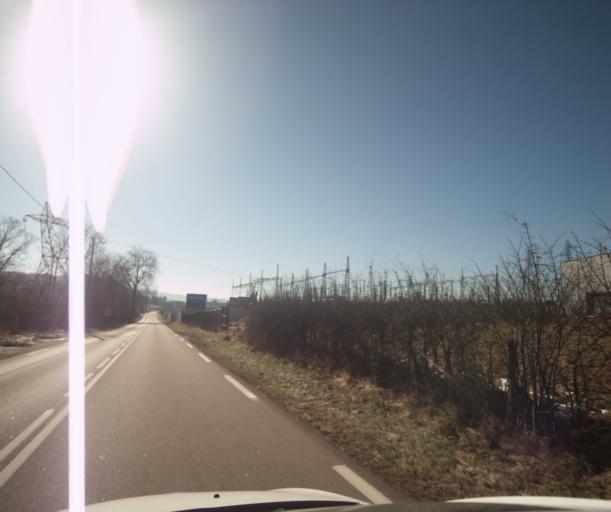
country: FR
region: Franche-Comte
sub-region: Departement du Doubs
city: Thise
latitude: 47.2691
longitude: 6.0557
